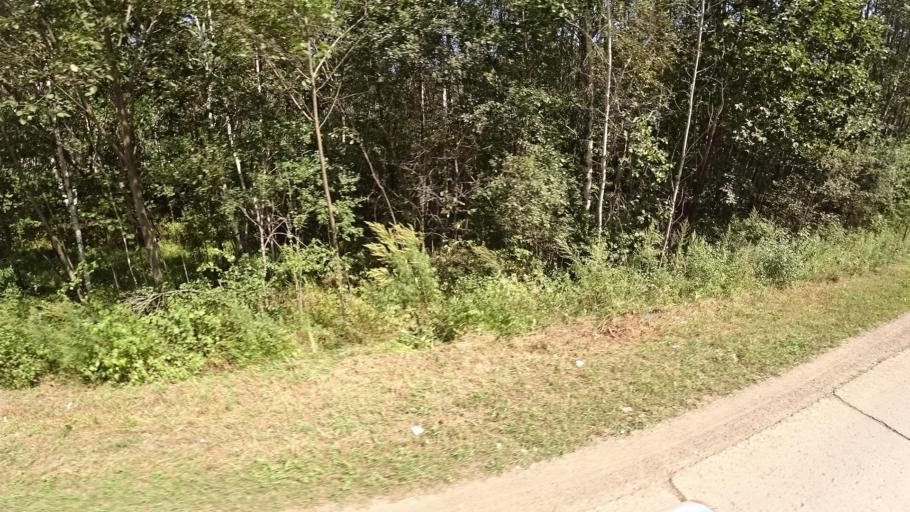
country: RU
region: Khabarovsk Krai
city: Khor
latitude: 47.9864
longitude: 135.0962
